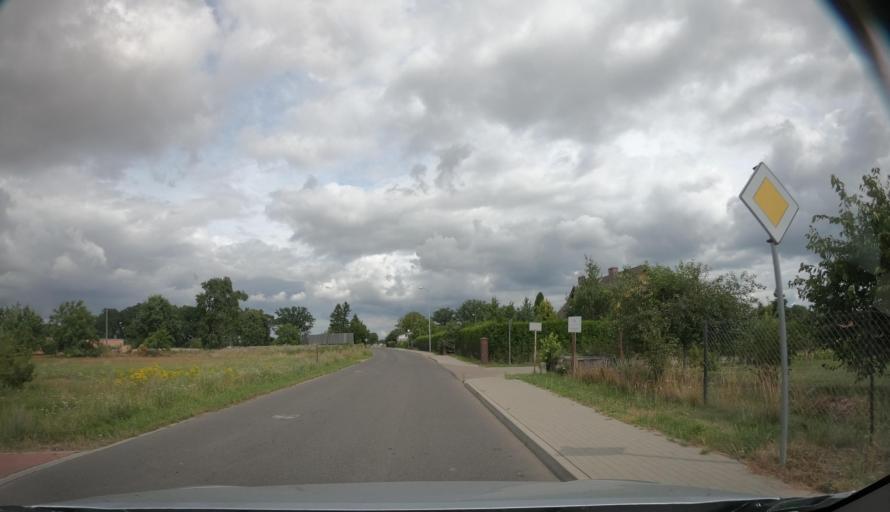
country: PL
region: West Pomeranian Voivodeship
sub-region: Koszalin
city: Koszalin
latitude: 54.1416
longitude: 16.0829
